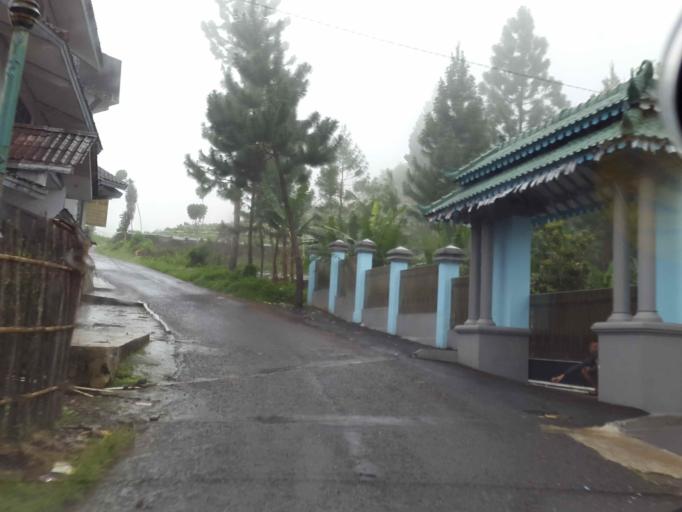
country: ID
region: Central Java
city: Baturaden
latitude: -7.1994
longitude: 109.1631
